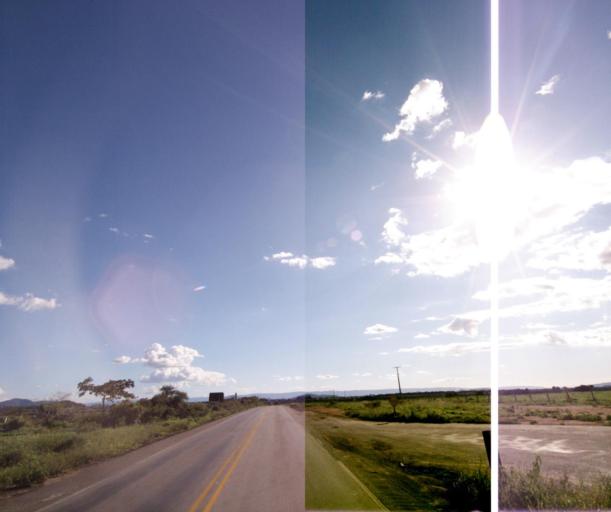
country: BR
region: Bahia
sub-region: Guanambi
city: Guanambi
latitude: -14.1777
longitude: -42.7317
